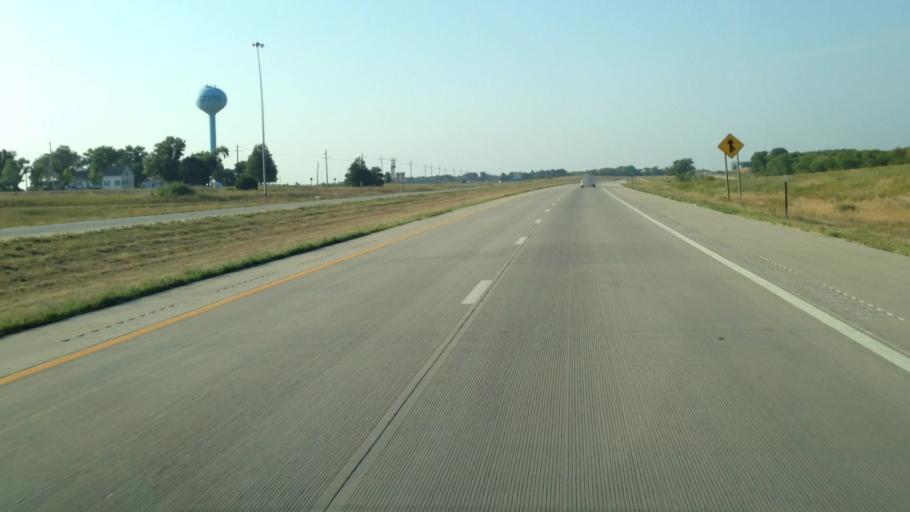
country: US
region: Kansas
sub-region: Douglas County
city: Baldwin City
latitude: 38.8342
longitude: -95.2688
